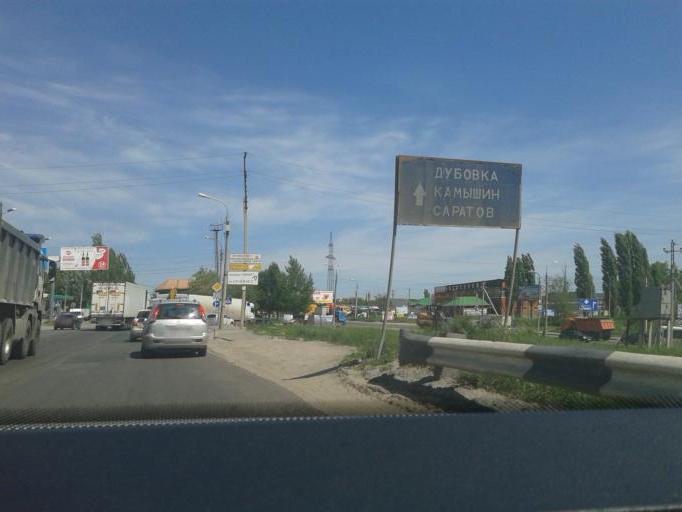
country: RU
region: Volgograd
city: Gorodishche
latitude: 48.7751
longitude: 44.5196
